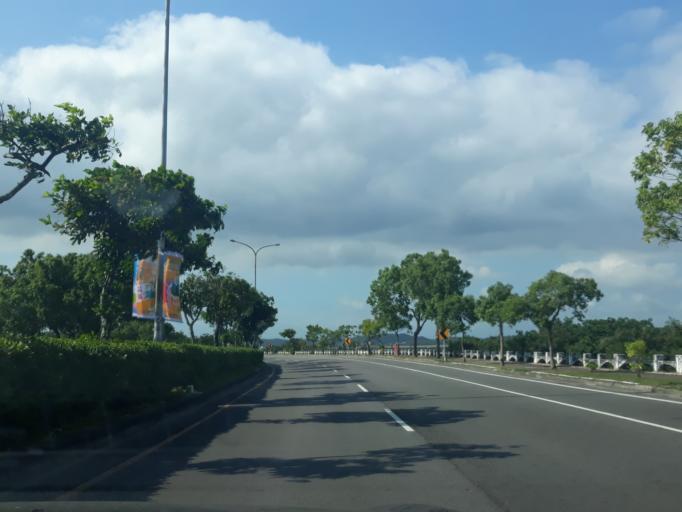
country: TW
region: Taiwan
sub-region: Miaoli
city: Miaoli
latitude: 24.5840
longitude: 120.8424
